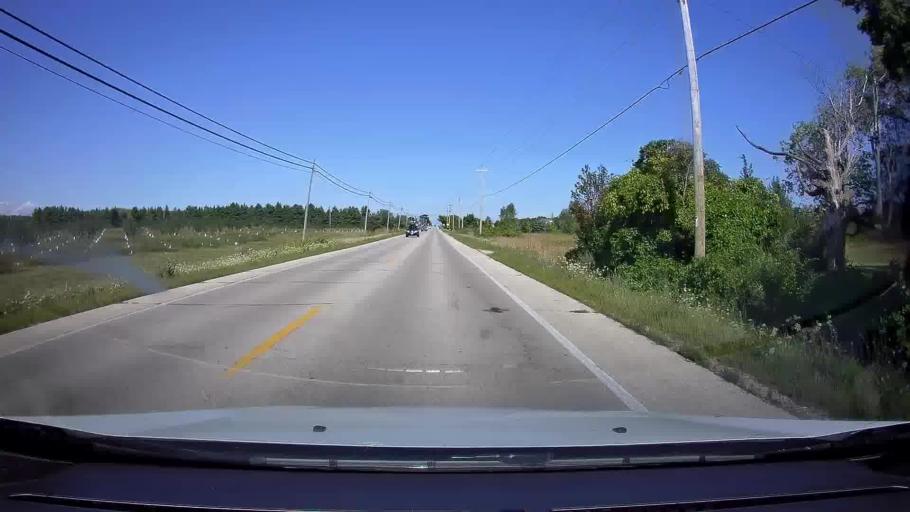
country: US
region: Wisconsin
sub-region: Door County
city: Sturgeon Bay
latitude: 45.2420
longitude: -87.0891
